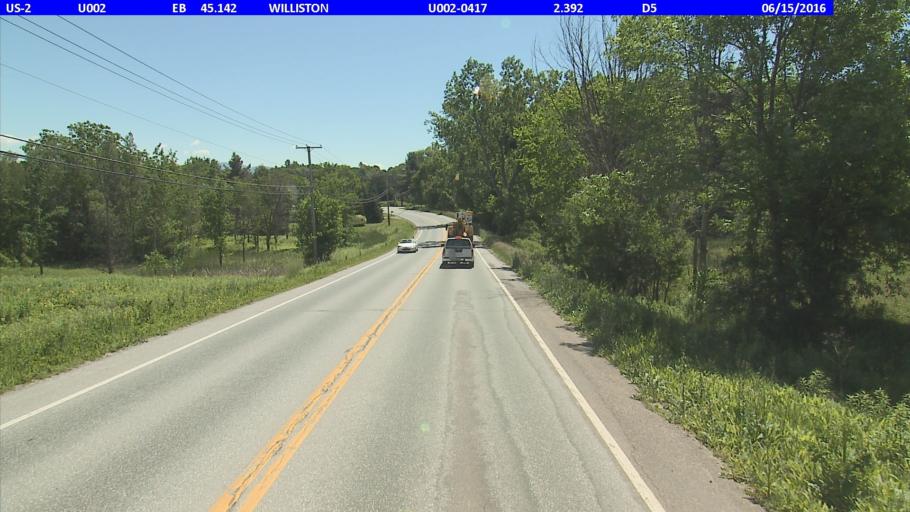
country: US
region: Vermont
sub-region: Chittenden County
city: Williston
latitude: 44.4429
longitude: -73.0938
